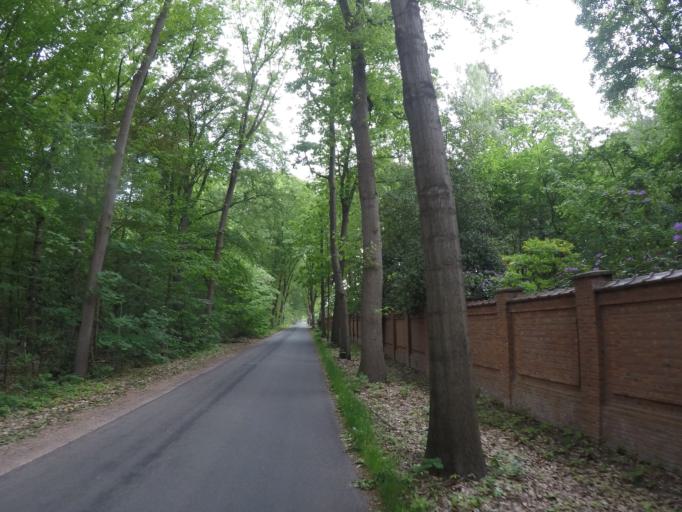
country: BE
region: Flanders
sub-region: Provincie Antwerpen
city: Zoersel
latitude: 51.2797
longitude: 4.6541
